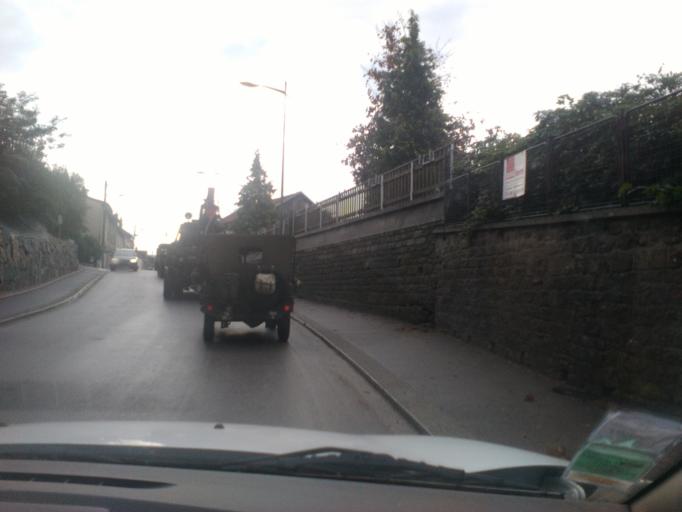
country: FR
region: Lorraine
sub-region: Departement des Vosges
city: Bruyeres
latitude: 48.2124
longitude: 6.7134
